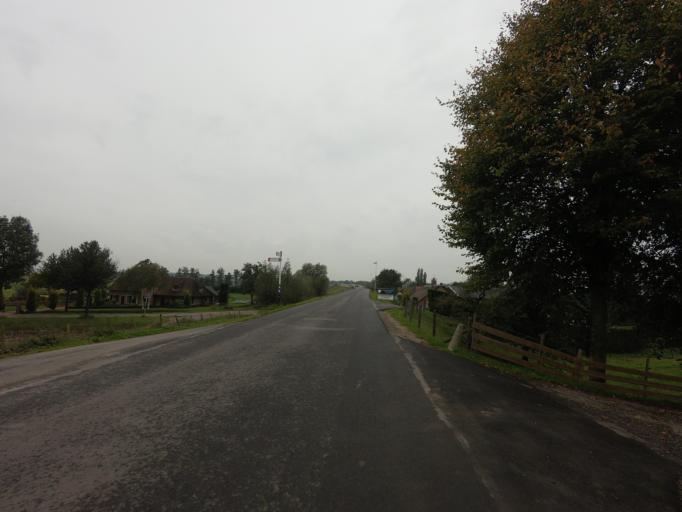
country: NL
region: Gelderland
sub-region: Gemeente Culemborg
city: Culemborg
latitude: 51.9401
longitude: 5.1565
